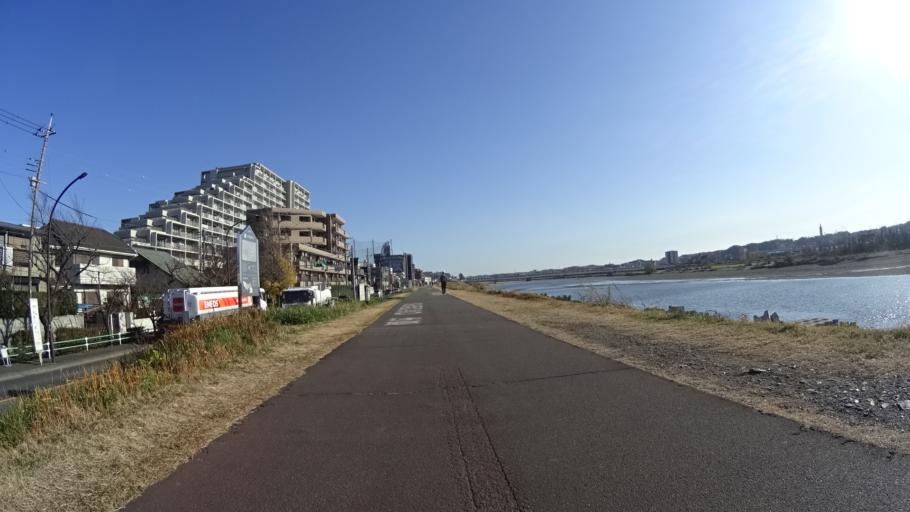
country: JP
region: Tokyo
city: Chofugaoka
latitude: 35.6503
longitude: 139.5202
